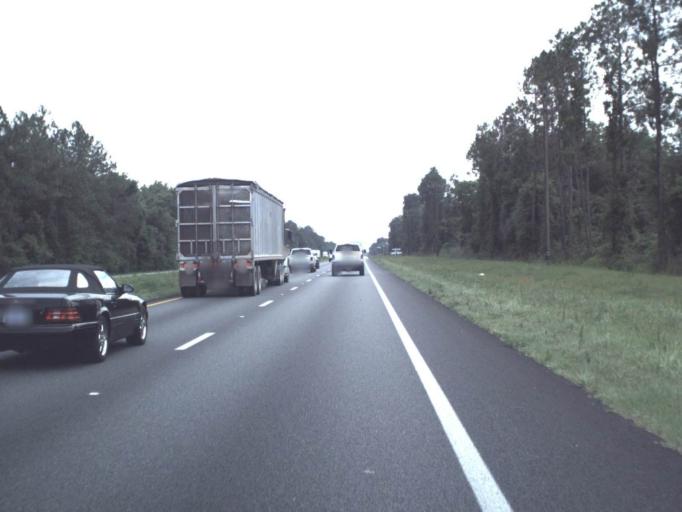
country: US
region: Florida
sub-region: Duval County
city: Baldwin
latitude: 30.1689
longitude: -82.0267
